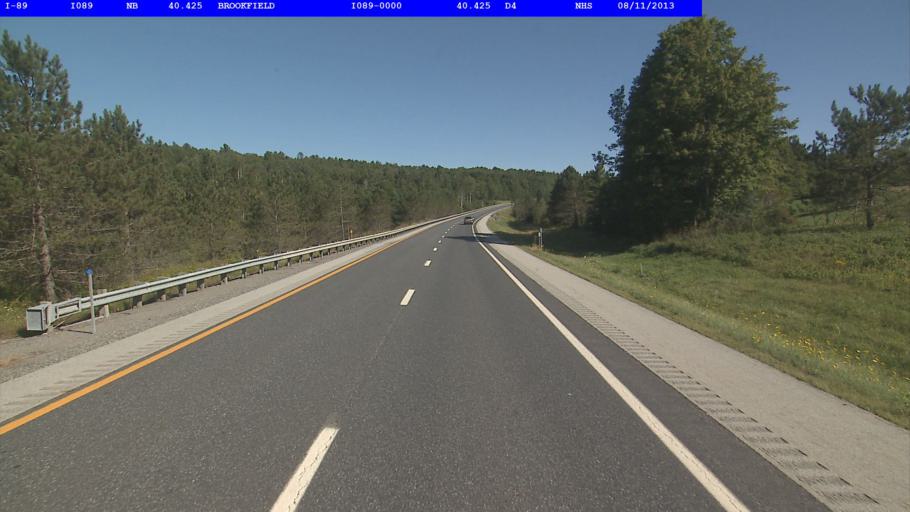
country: US
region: Vermont
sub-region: Orange County
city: Williamstown
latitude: 44.0794
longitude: -72.6123
